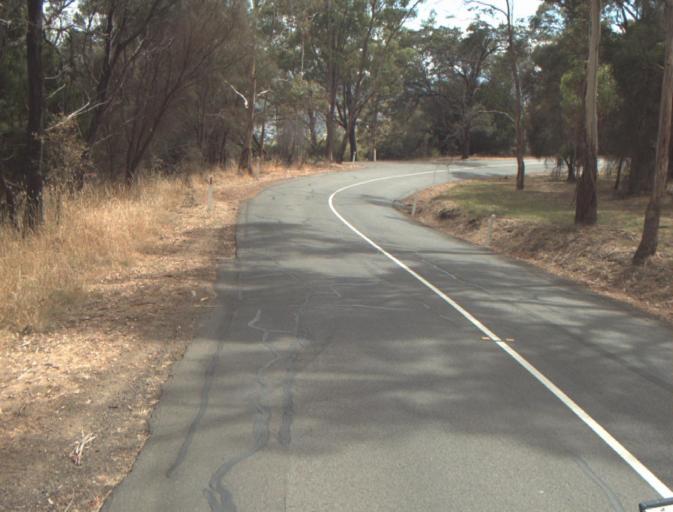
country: AU
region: Tasmania
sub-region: Launceston
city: West Launceston
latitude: -41.4502
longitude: 147.1197
